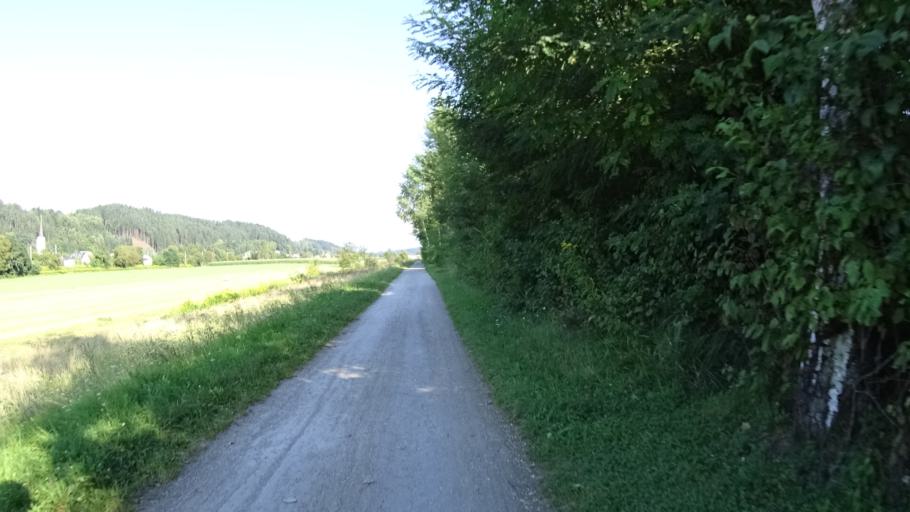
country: AT
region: Carinthia
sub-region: Politischer Bezirk Villach Land
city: Wernberg
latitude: 46.6130
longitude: 13.9310
